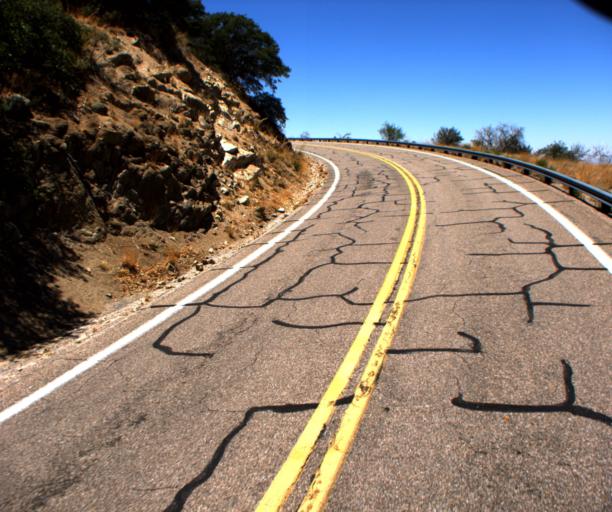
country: US
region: Arizona
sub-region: Pima County
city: Sells
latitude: 31.9754
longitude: -111.6065
